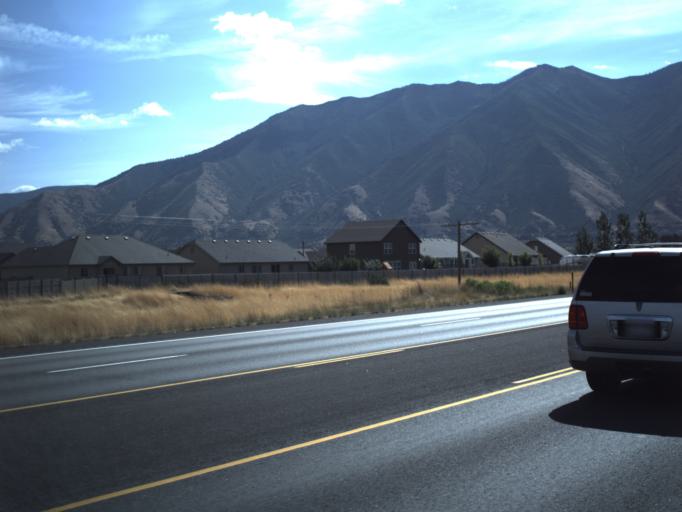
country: US
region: Utah
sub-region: Utah County
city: Spanish Fork
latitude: 40.1032
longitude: -111.6197
